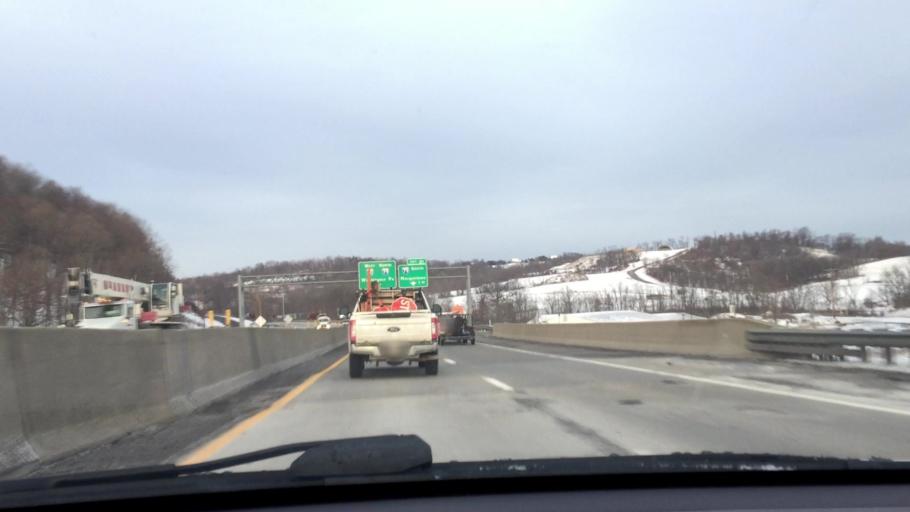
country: US
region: Pennsylvania
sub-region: Washington County
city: East Washington
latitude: 40.1669
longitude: -80.1716
